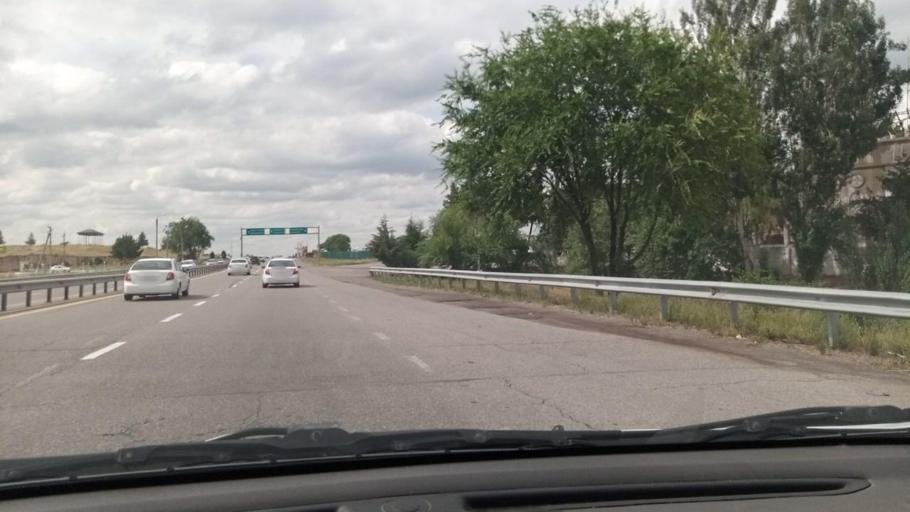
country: UZ
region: Toshkent
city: Tuytepa
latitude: 41.1194
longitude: 69.4427
